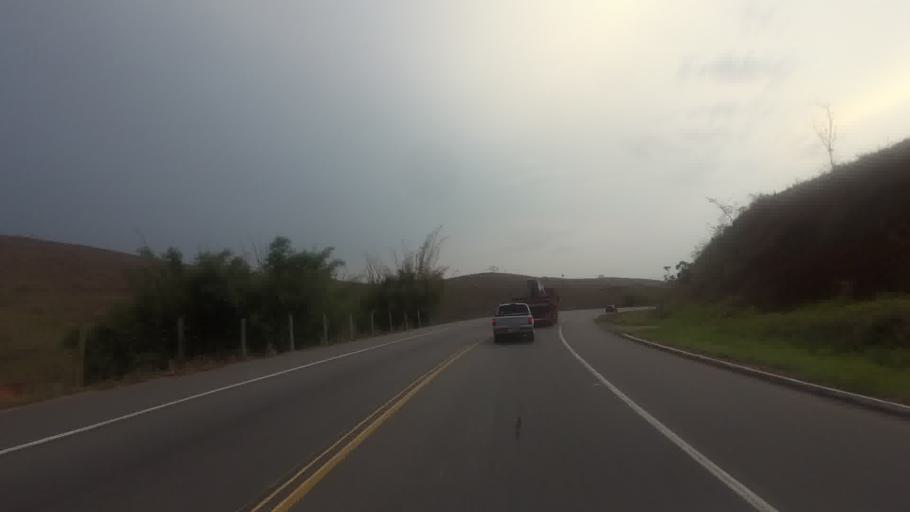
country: BR
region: Rio de Janeiro
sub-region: Carmo
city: Carmo
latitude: -21.8121
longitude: -42.5939
